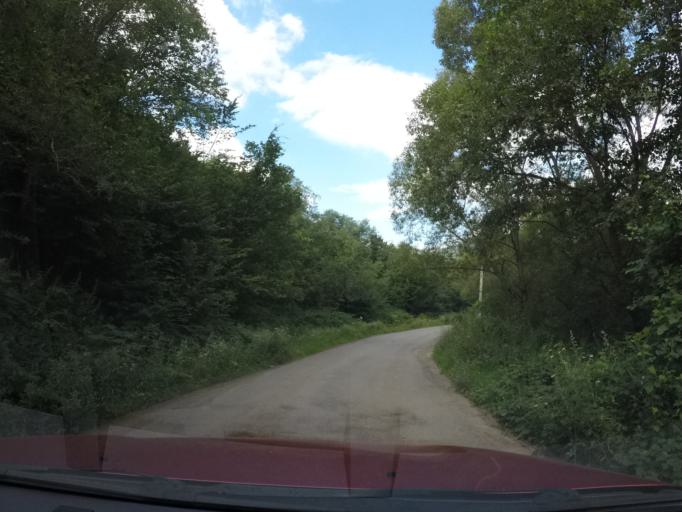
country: UA
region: Zakarpattia
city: Velykyi Bereznyi
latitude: 48.9509
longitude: 22.6667
